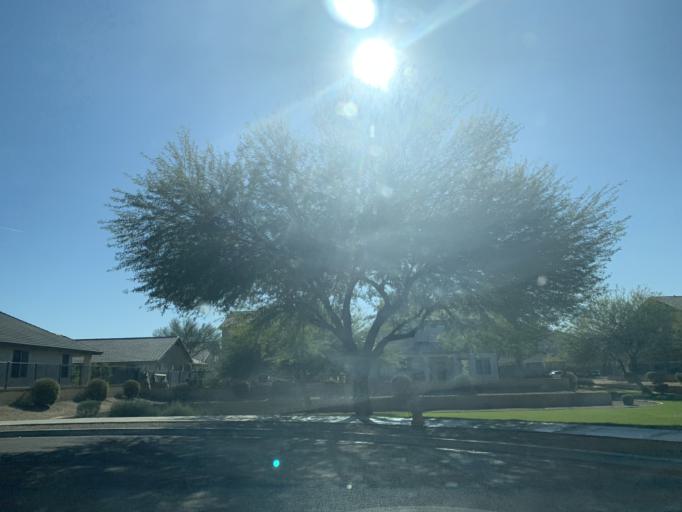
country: US
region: Arizona
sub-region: Maricopa County
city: Laveen
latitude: 33.3982
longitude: -112.1312
